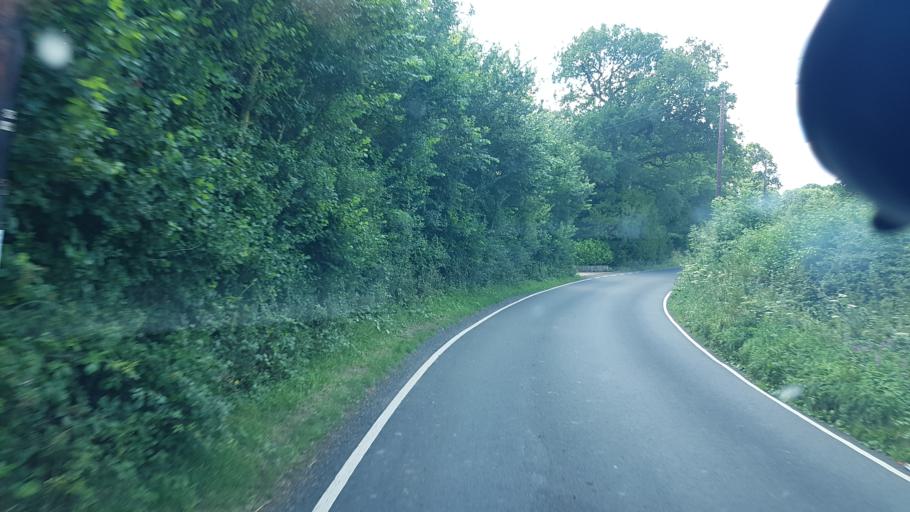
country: GB
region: England
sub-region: Kent
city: Edenbridge
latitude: 51.2145
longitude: 0.1317
